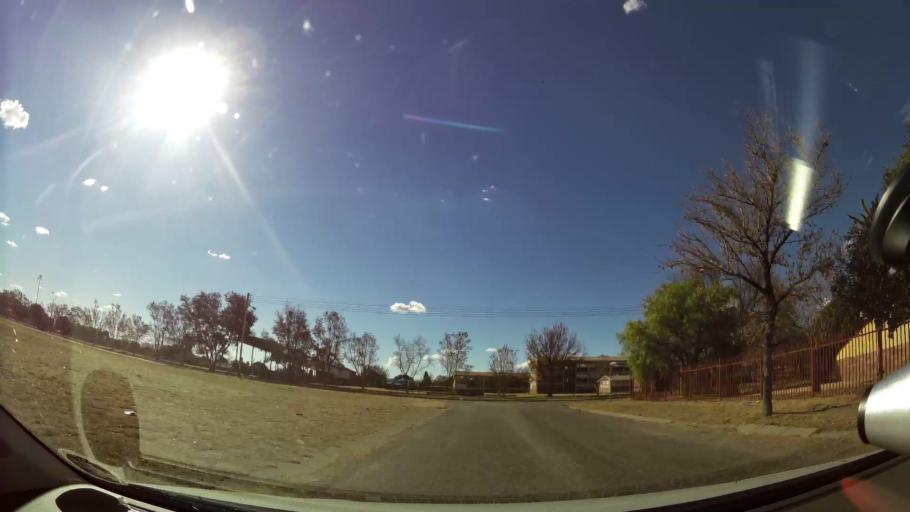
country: ZA
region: North-West
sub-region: Dr Kenneth Kaunda District Municipality
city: Klerksdorp
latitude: -26.8293
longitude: 26.6533
